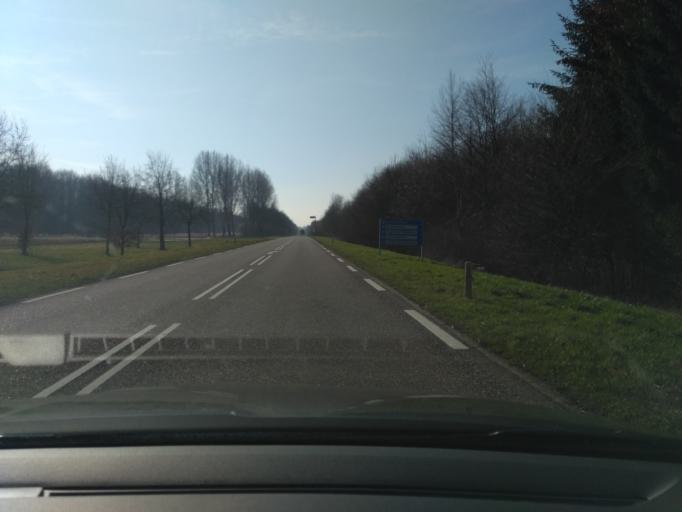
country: NL
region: Flevoland
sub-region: Gemeente Zeewolde
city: Zeewolde
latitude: 52.3111
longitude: 5.5181
